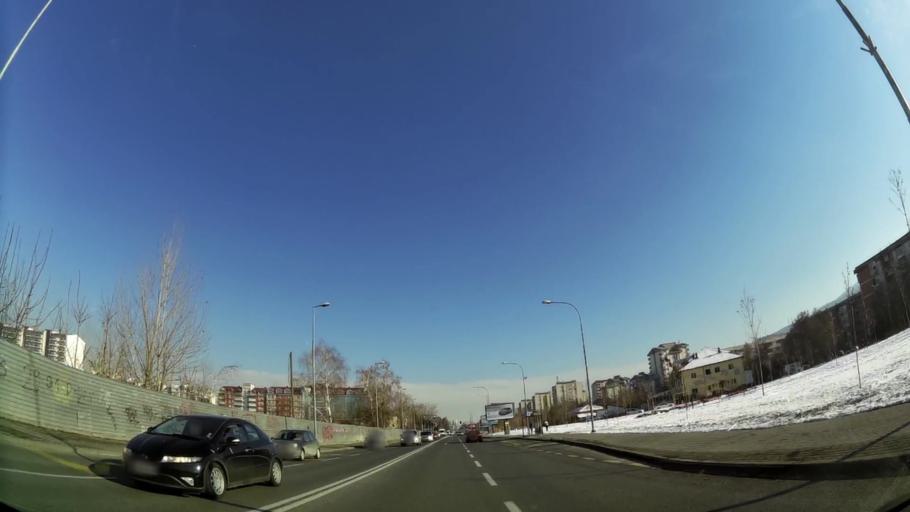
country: MK
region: Karpos
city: Skopje
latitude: 41.9968
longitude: 21.4010
